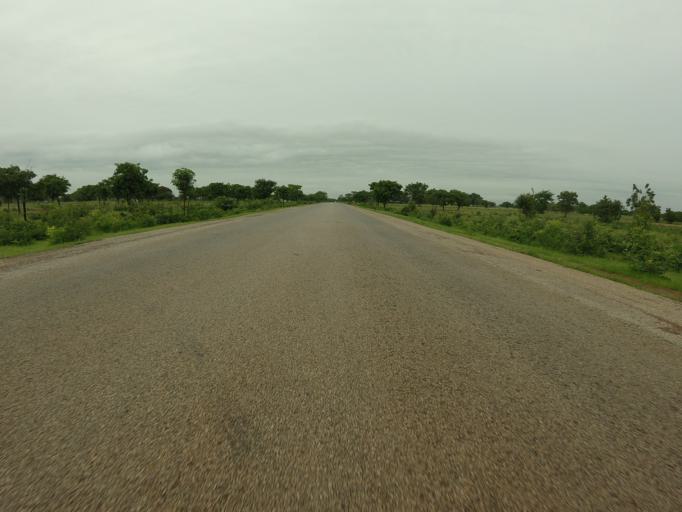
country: GH
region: Northern
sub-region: Yendi
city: Yendi
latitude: 9.5118
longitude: -0.0282
